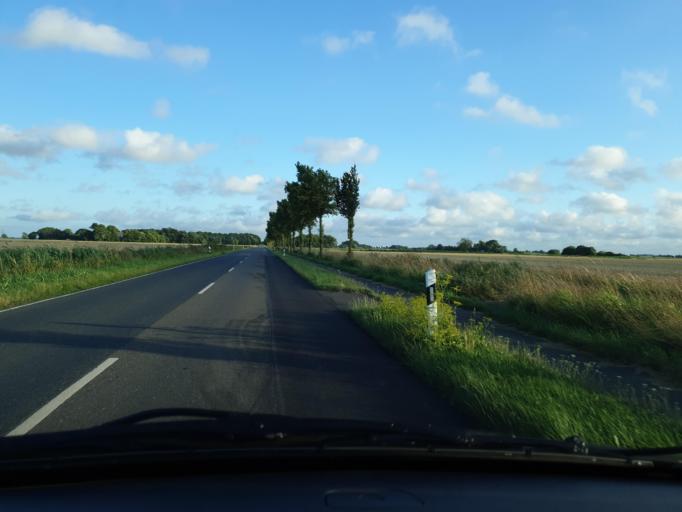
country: DE
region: Schleswig-Holstein
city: Wohrden
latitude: 54.1393
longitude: 9.0166
